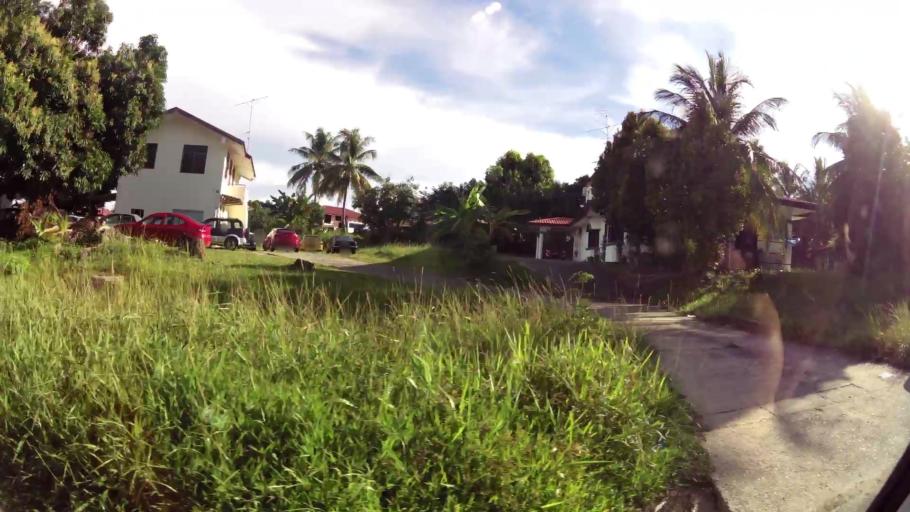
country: BN
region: Brunei and Muara
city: Bandar Seri Begawan
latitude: 4.9804
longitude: 114.9675
